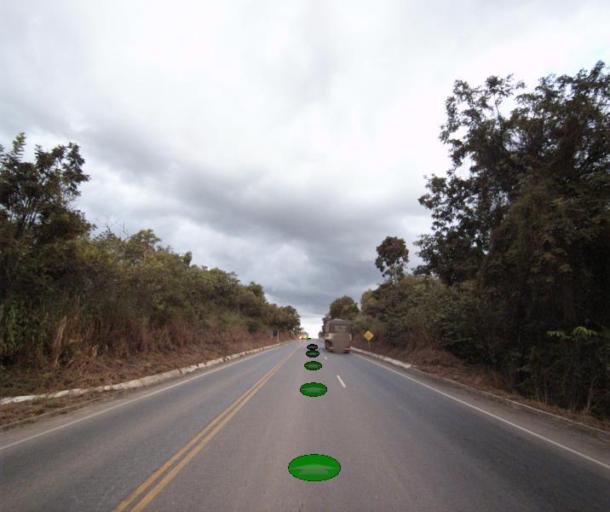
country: BR
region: Goias
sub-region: Uruacu
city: Uruacu
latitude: -14.7159
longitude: -49.2286
